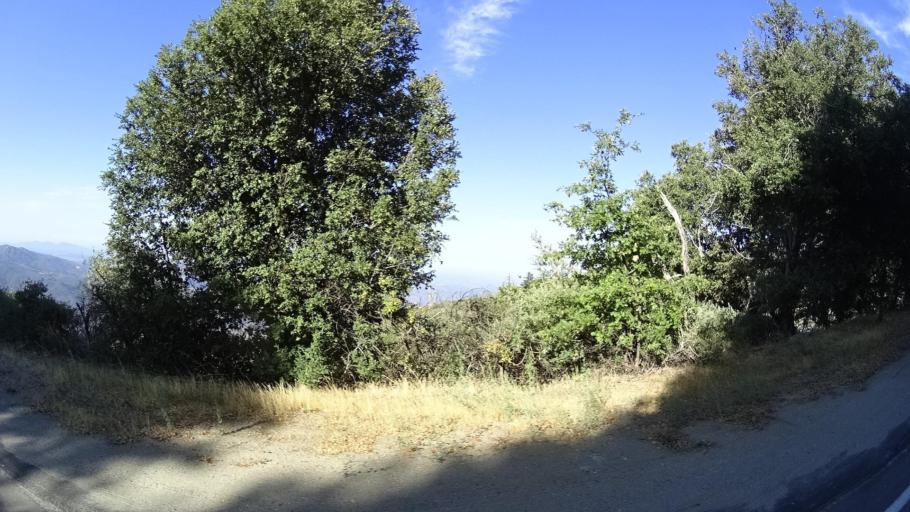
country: US
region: California
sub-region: Riverside County
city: Aguanga
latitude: 33.3001
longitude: -116.8427
